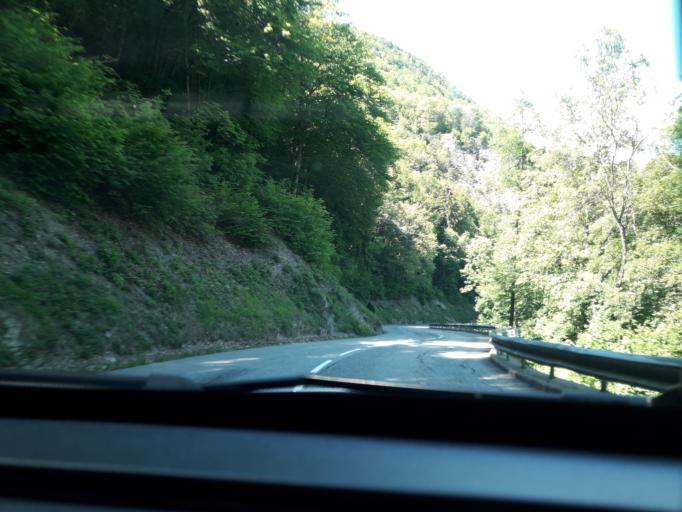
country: FR
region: Rhone-Alpes
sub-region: Departement de la Savoie
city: Salins-les-Thermes
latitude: 45.4761
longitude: 6.5246
